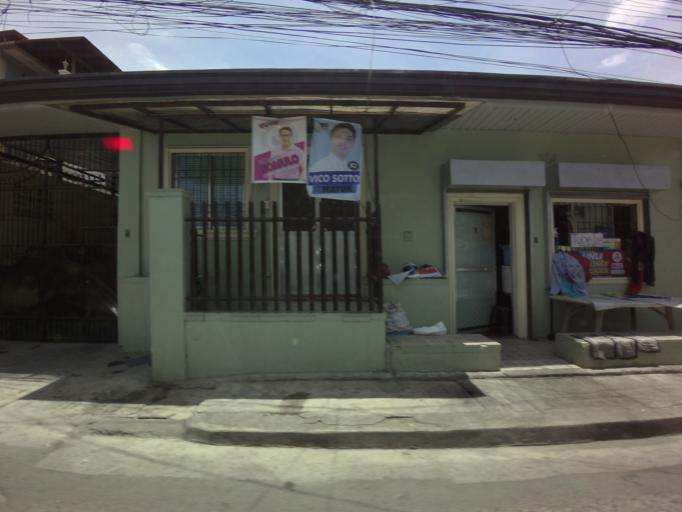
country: PH
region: Metro Manila
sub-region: Marikina
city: Calumpang
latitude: 14.6164
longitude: 121.0841
